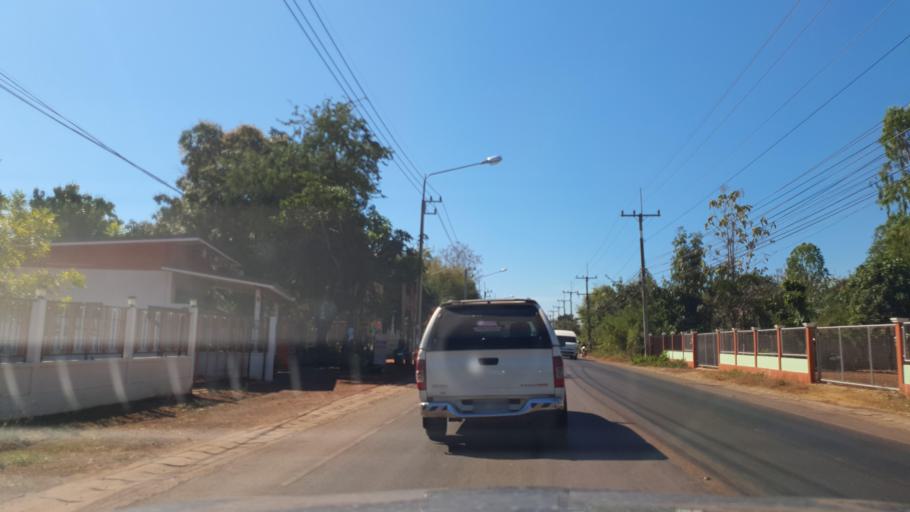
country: TH
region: Sakon Nakhon
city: Phon Na Kaeo
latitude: 17.2629
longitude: 104.1910
